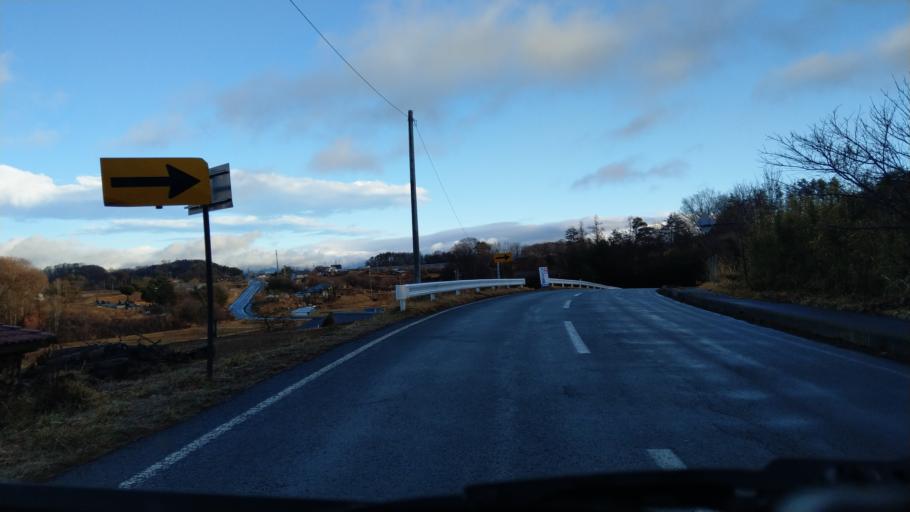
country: JP
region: Nagano
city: Komoro
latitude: 36.3072
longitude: 138.3938
